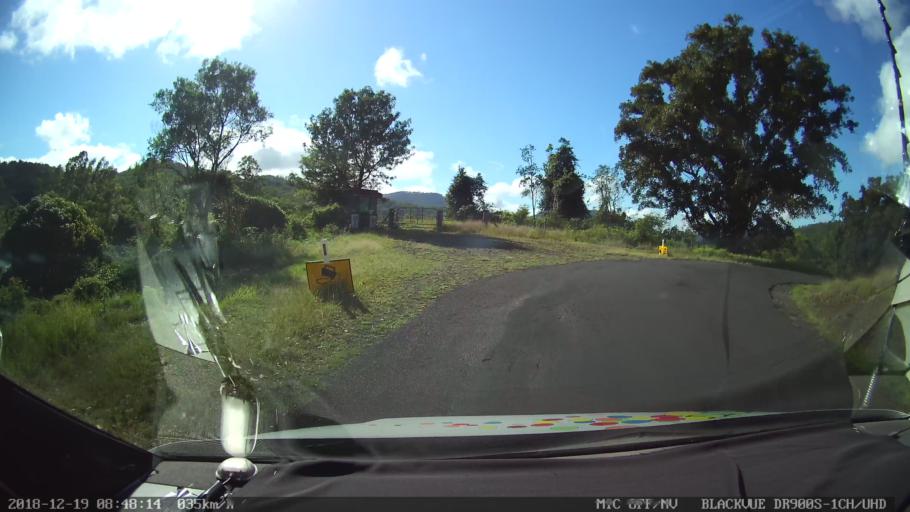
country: AU
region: New South Wales
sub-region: Kyogle
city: Kyogle
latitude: -28.3708
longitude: 152.9725
